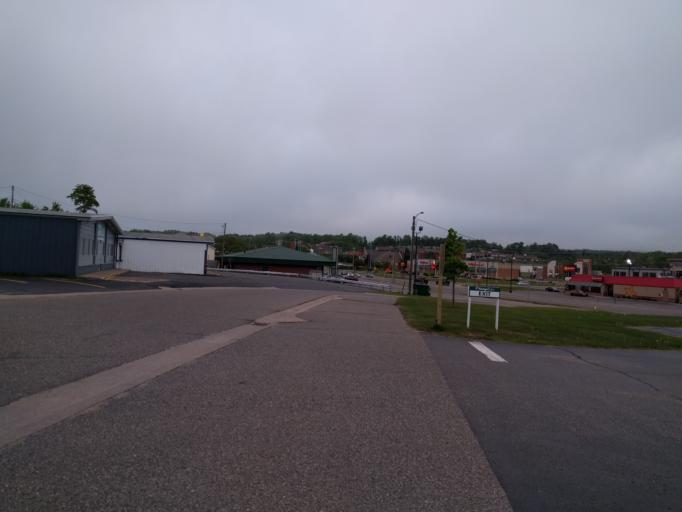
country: US
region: Michigan
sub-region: Marquette County
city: Trowbridge Park
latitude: 46.5473
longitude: -87.4189
